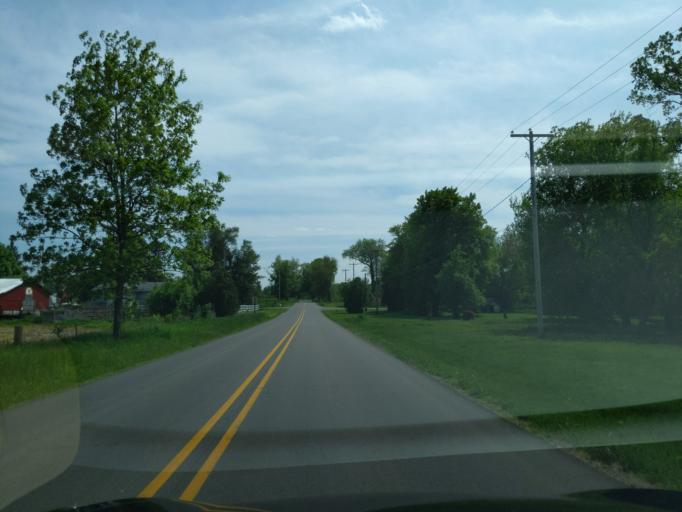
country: US
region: Michigan
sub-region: Ingham County
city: Leslie
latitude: 42.4123
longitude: -84.3138
